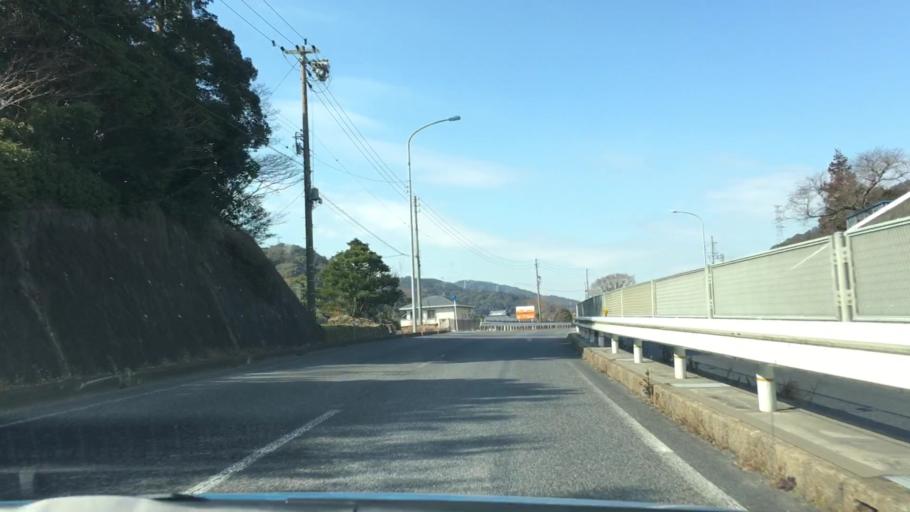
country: JP
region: Aichi
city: Gamagori
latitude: 34.8692
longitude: 137.2898
